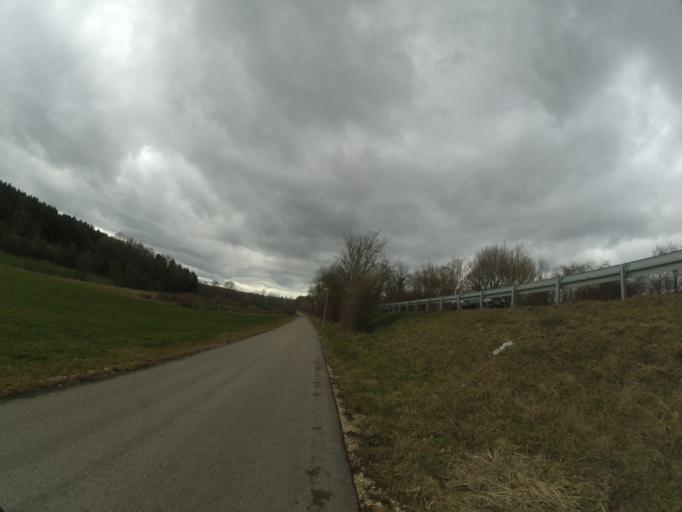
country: DE
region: Bavaria
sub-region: Swabia
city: Vohringen
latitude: 48.3178
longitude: 10.0871
